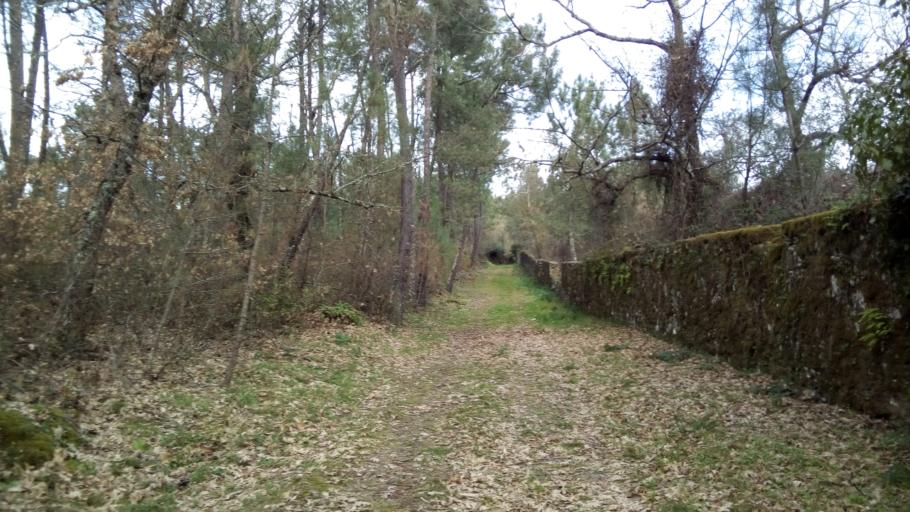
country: PT
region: Guarda
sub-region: Fornos de Algodres
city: Fornos de Algodres
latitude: 40.6120
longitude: -7.5300
